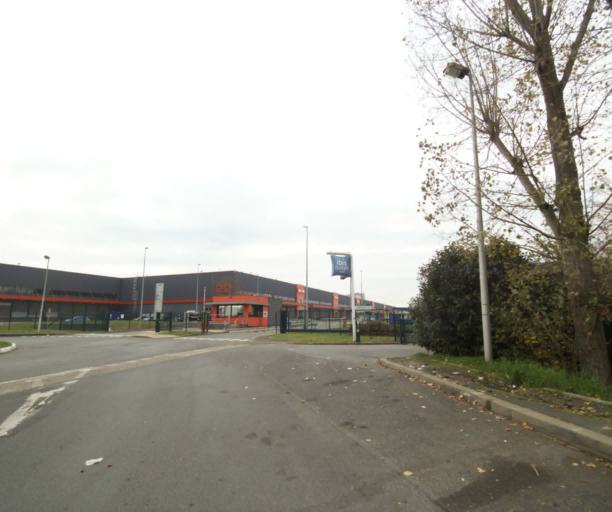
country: FR
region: Ile-de-France
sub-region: Departement de Seine-Saint-Denis
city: Le Blanc-Mesnil
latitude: 48.9538
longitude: 2.4572
